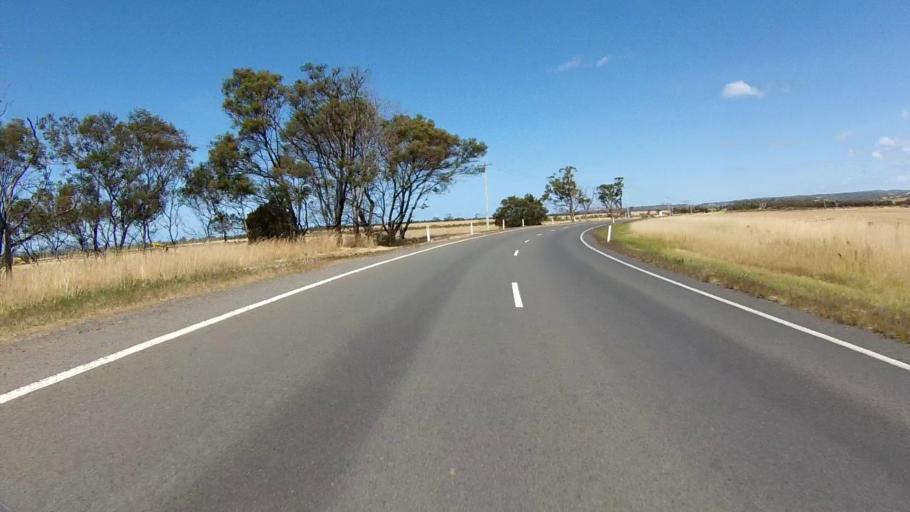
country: AU
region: Tasmania
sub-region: Break O'Day
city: St Helens
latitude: -42.0877
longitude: 148.0671
